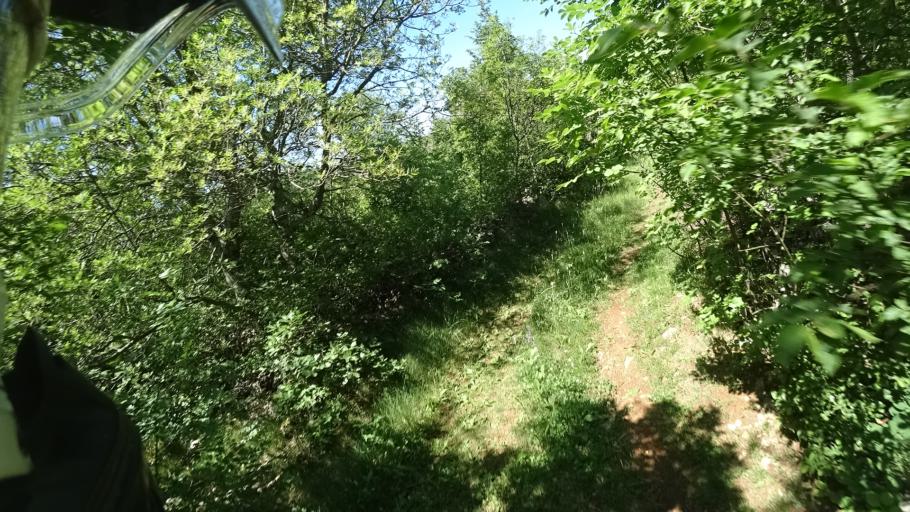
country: HR
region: Sibensko-Kniniska
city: Knin
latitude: 44.0176
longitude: 16.3578
